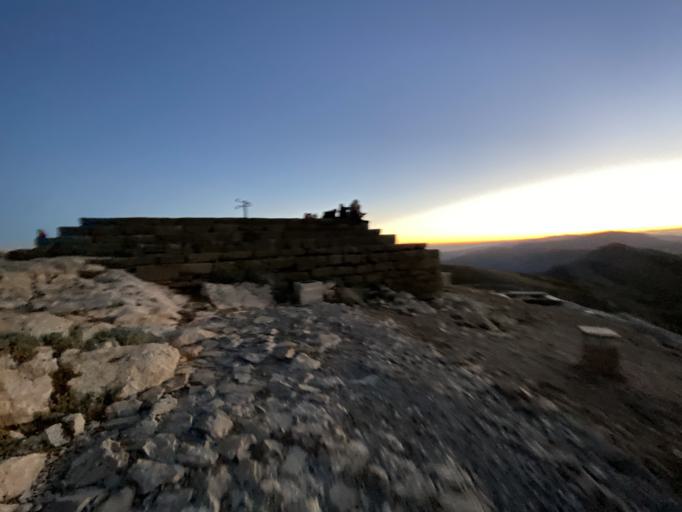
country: TR
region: Adiyaman
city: Narince
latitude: 37.9809
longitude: 38.7420
